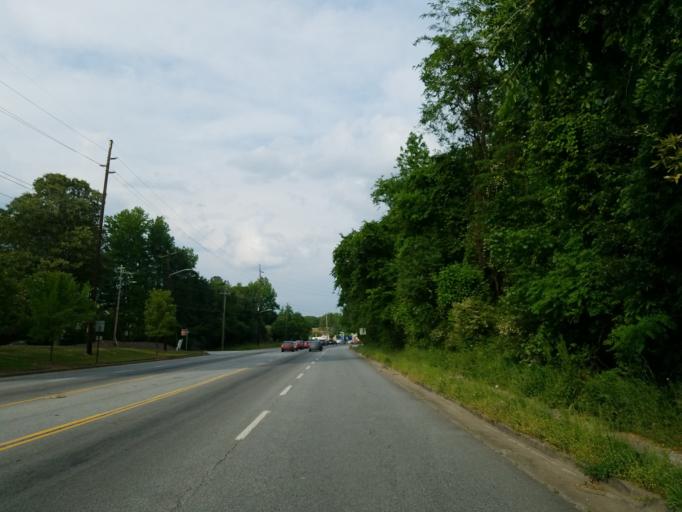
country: US
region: Georgia
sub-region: Cobb County
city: Vinings
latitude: 33.8098
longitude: -84.4787
